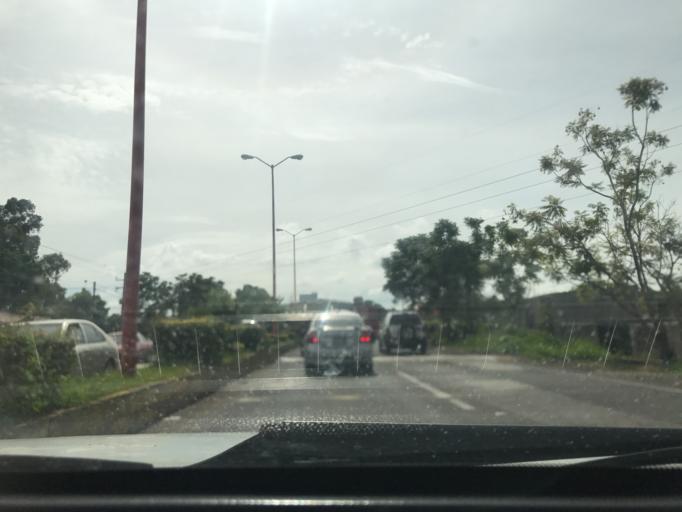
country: MX
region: Morelos
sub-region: Atlatlahucan
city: Colonia San Francisco
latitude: 18.8954
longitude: -98.9039
